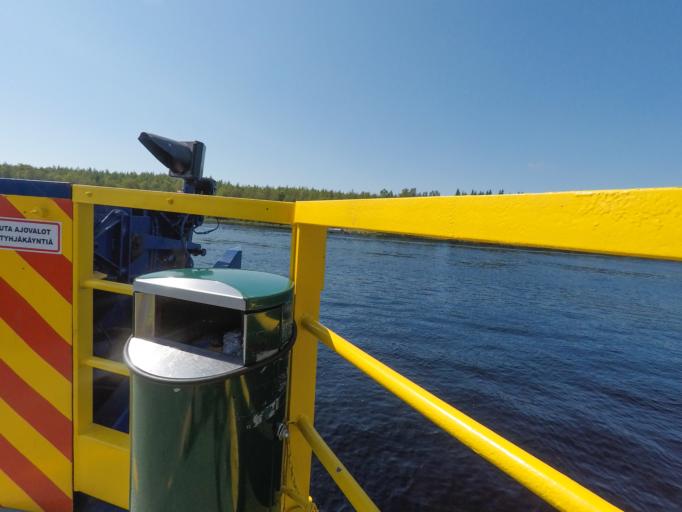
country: FI
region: Southern Savonia
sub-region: Mikkeli
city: Puumala
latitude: 61.4522
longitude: 28.1679
